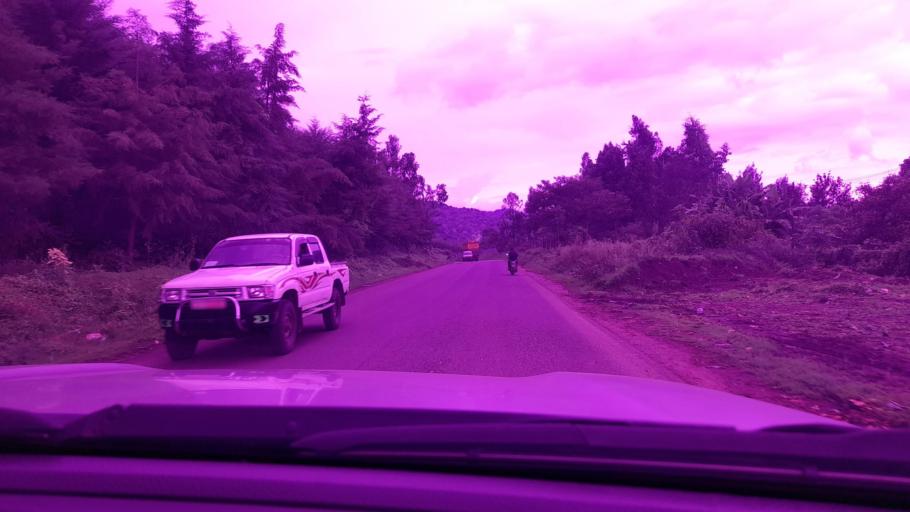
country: ET
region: Oromiya
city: Jima
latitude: 7.6632
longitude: 36.8741
